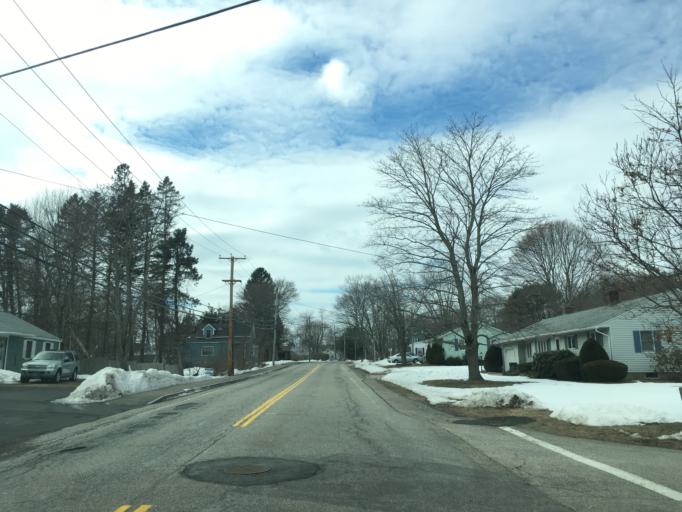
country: US
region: New Hampshire
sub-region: Rockingham County
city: Hampton
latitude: 42.9383
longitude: -70.8221
